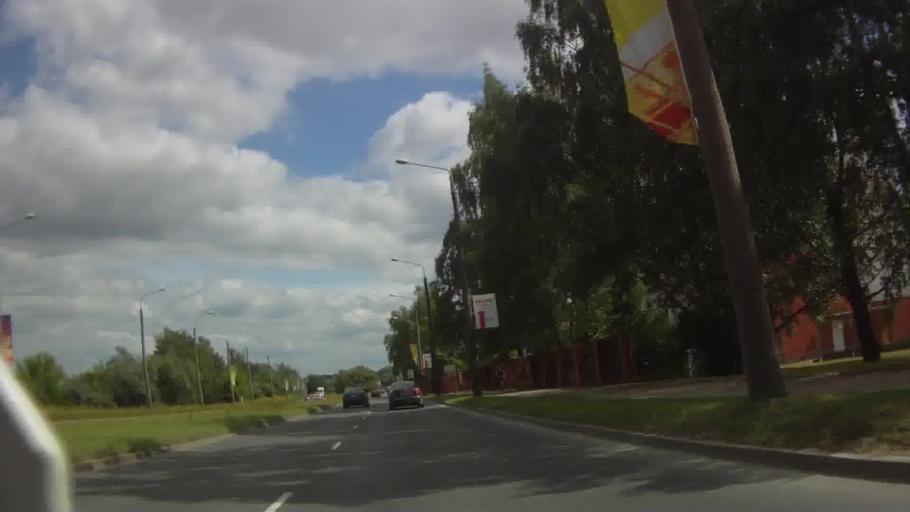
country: LV
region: Riga
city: Riga
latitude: 56.9192
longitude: 24.1125
